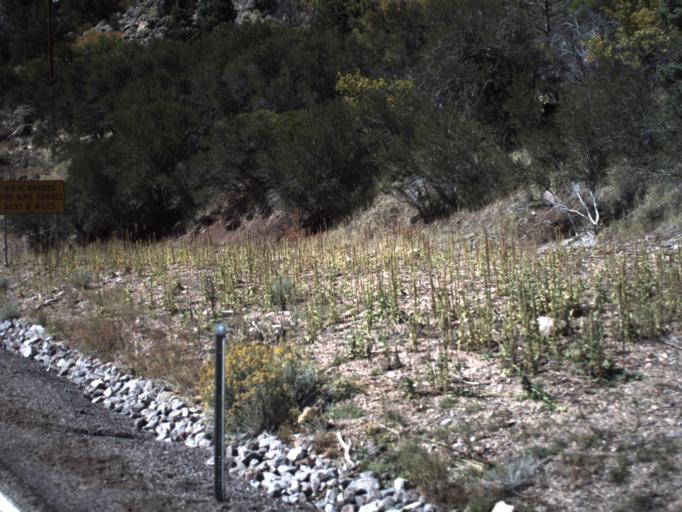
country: US
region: Utah
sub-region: Beaver County
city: Beaver
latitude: 38.2737
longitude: -112.4643
